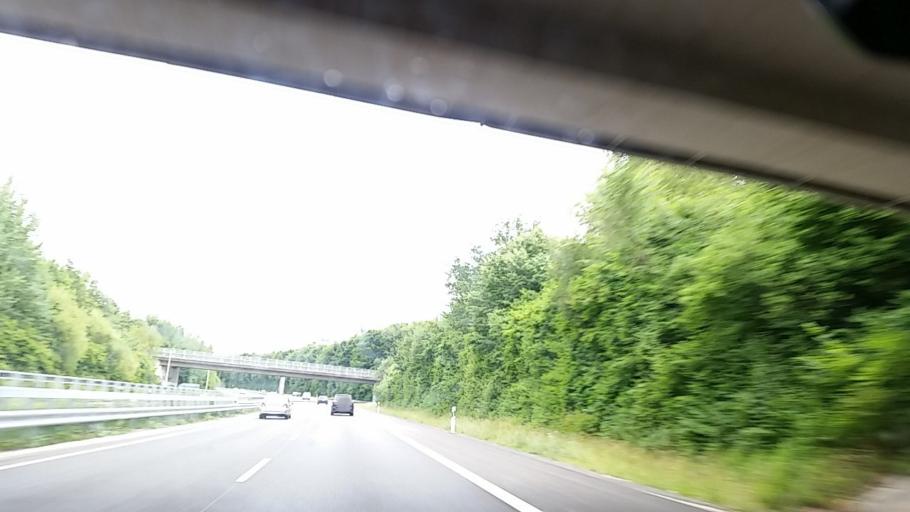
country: DE
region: Schleswig-Holstein
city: Kronshagen
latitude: 54.3572
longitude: 10.0944
